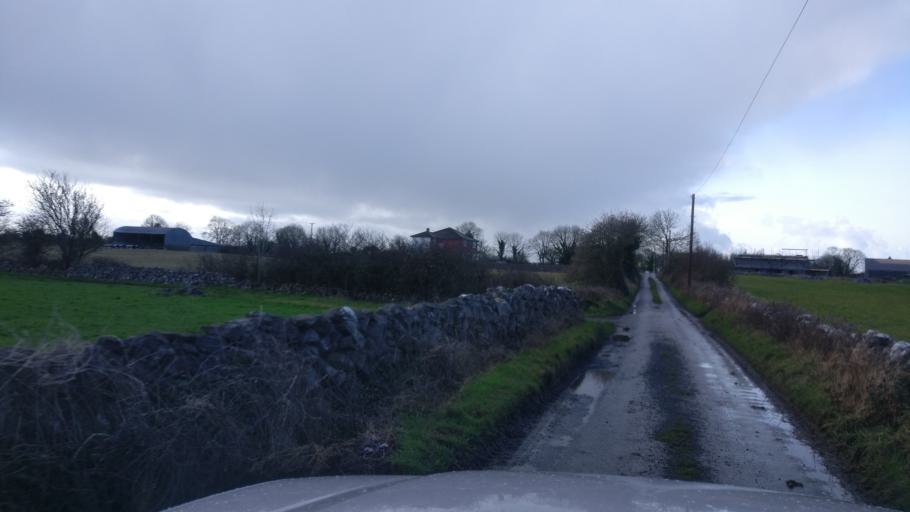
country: IE
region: Connaught
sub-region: County Galway
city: Oranmore
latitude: 53.2641
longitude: -8.8817
